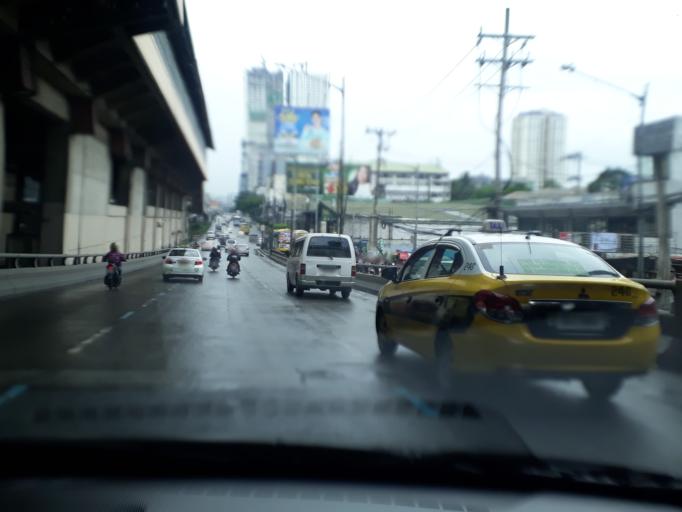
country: PH
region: Metro Manila
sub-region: Quezon City
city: Quezon City
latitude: 14.6429
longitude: 121.0383
